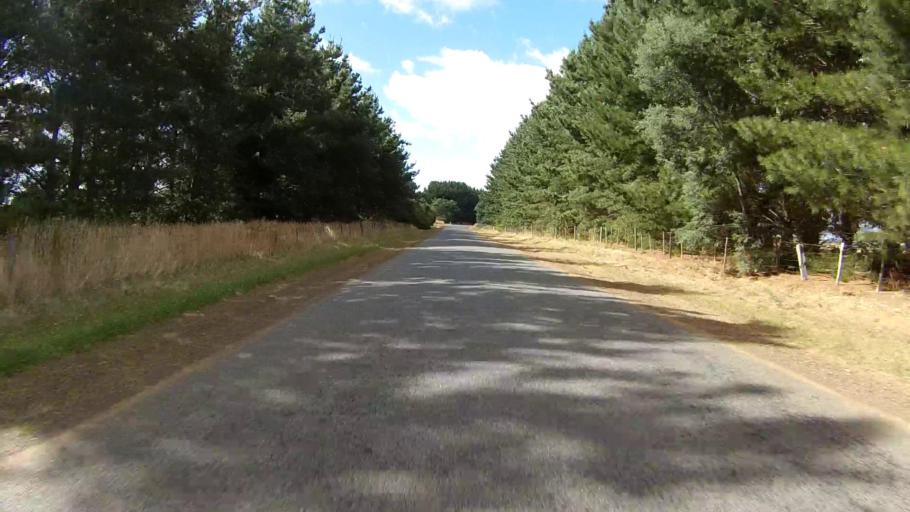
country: AU
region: Tasmania
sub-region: Northern Midlands
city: Evandale
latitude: -41.6920
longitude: 147.3647
